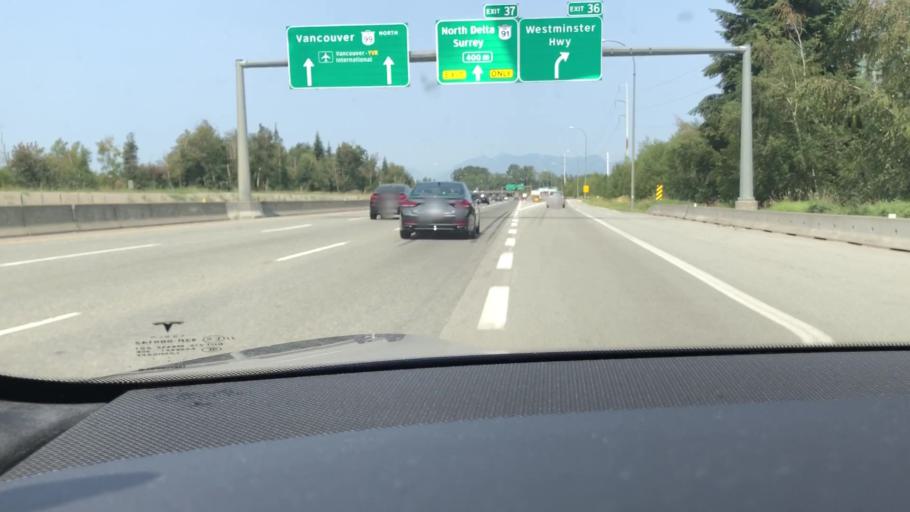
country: CA
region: British Columbia
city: Richmond
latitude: 49.1634
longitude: -123.0864
